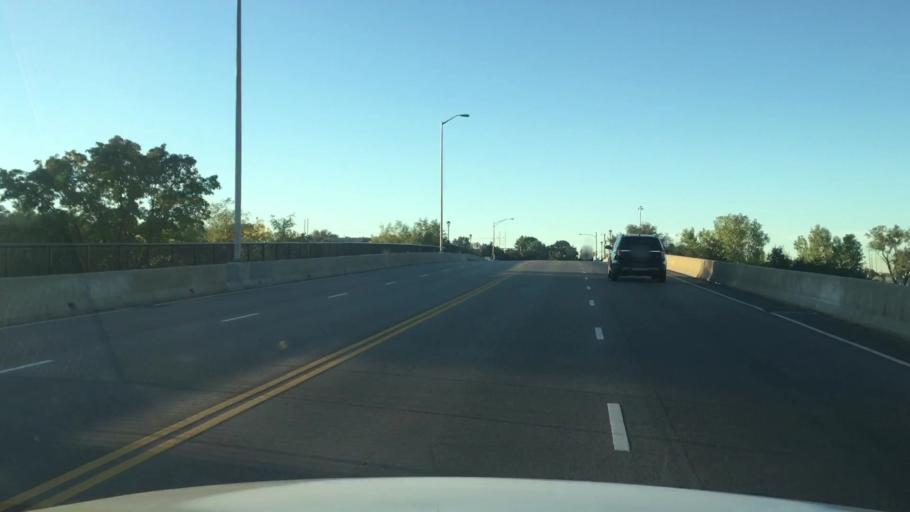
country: US
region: Kansas
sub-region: Johnson County
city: Merriam
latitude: 39.0372
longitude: -94.6866
